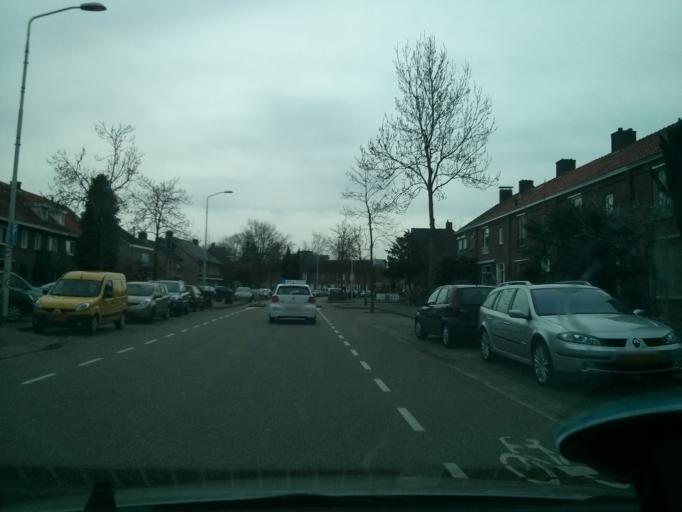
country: NL
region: North Brabant
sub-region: Gemeente Eindhoven
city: Eindhoven
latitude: 51.4718
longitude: 5.4831
